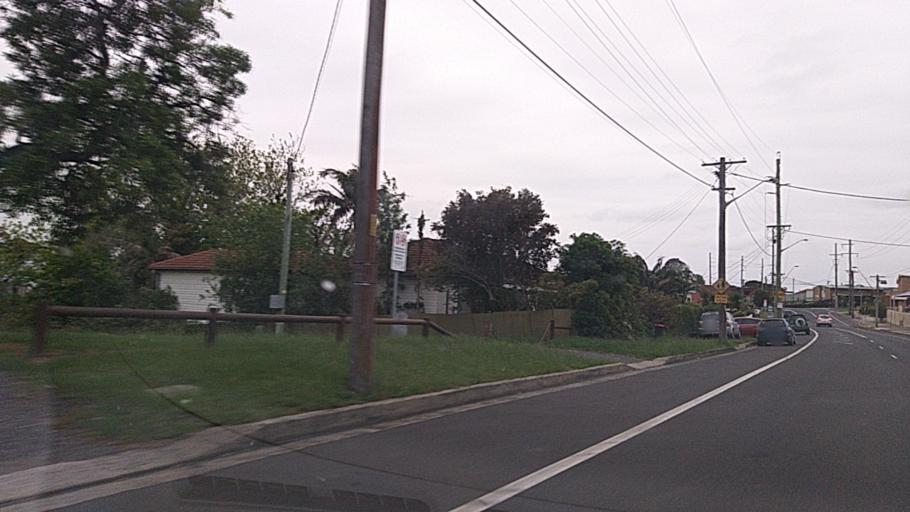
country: AU
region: New South Wales
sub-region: Wollongong
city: Lake Heights
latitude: -34.4796
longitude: 150.8785
